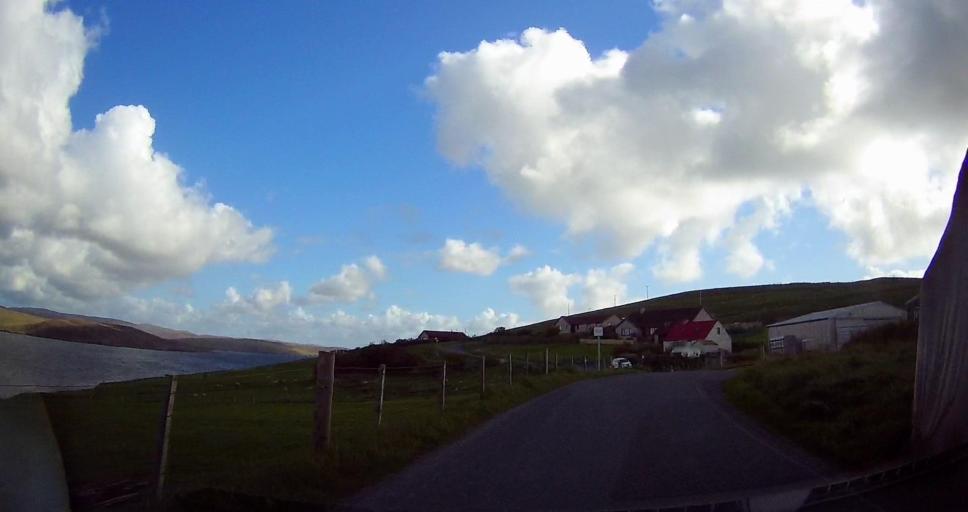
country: GB
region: Scotland
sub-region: Shetland Islands
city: Lerwick
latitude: 60.3735
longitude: -1.3819
